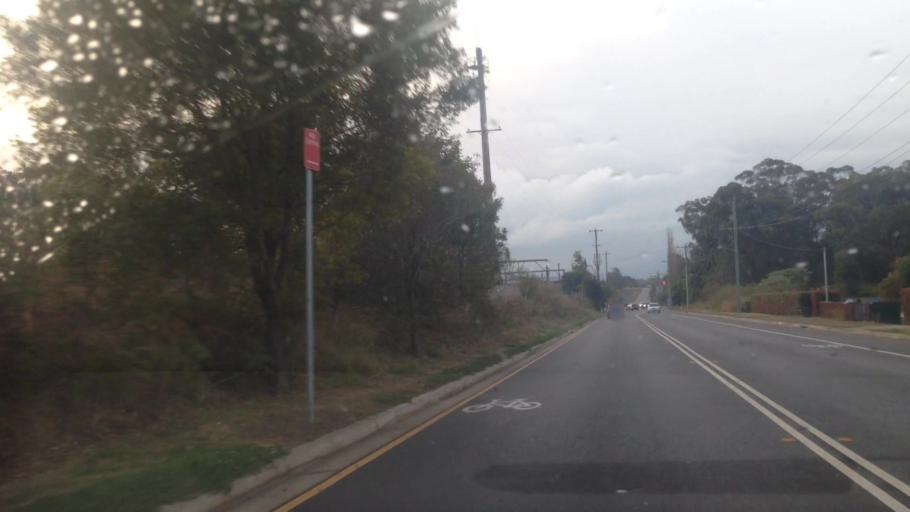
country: AU
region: New South Wales
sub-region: Wyong Shire
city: Charmhaven
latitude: -33.1824
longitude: 151.4875
